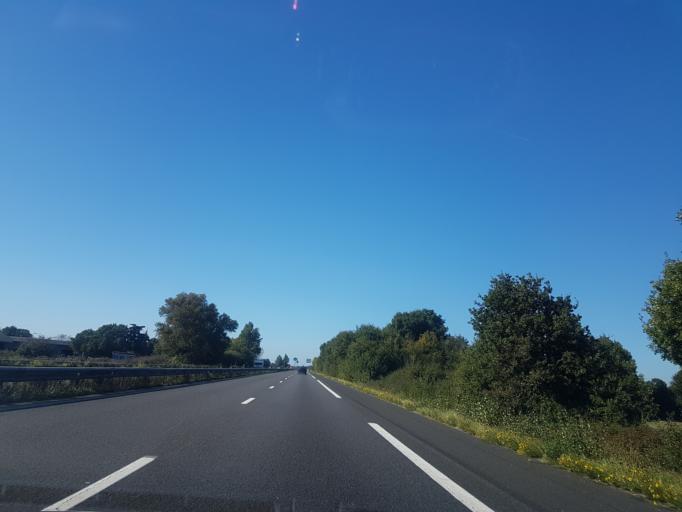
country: FR
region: Pays de la Loire
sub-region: Departement de la Loire-Atlantique
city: Donges
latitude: 47.3437
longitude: -2.0905
